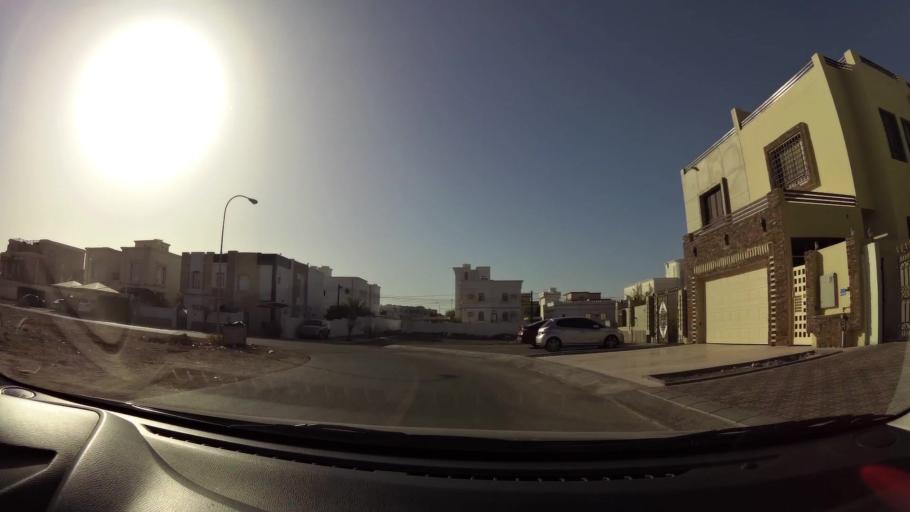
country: OM
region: Muhafazat Masqat
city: As Sib al Jadidah
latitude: 23.5956
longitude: 58.2052
